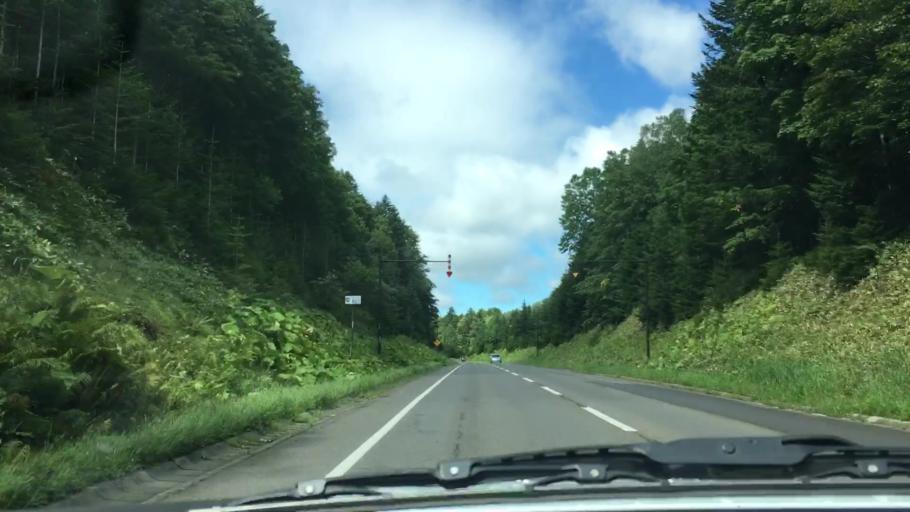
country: JP
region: Hokkaido
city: Bihoro
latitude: 43.4402
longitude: 144.0508
